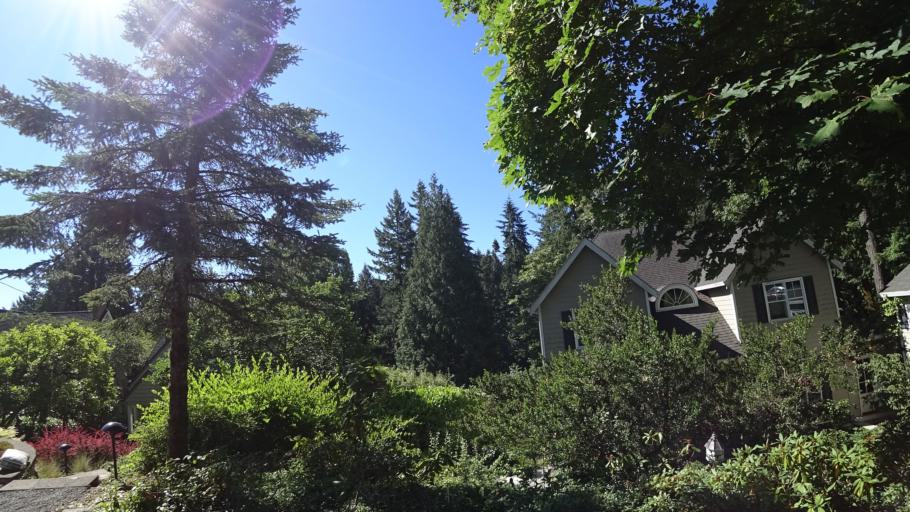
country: US
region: Oregon
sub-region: Multnomah County
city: Portland
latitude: 45.5023
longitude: -122.7036
